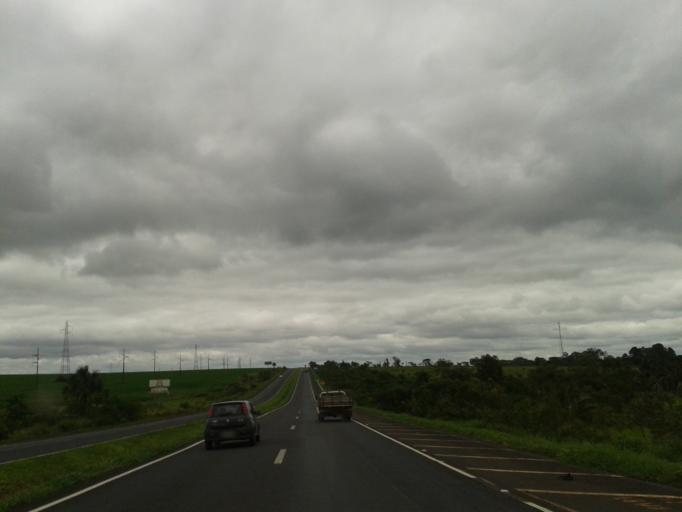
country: BR
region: Minas Gerais
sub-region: Uberlandia
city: Uberlandia
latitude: -19.0331
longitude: -48.2015
